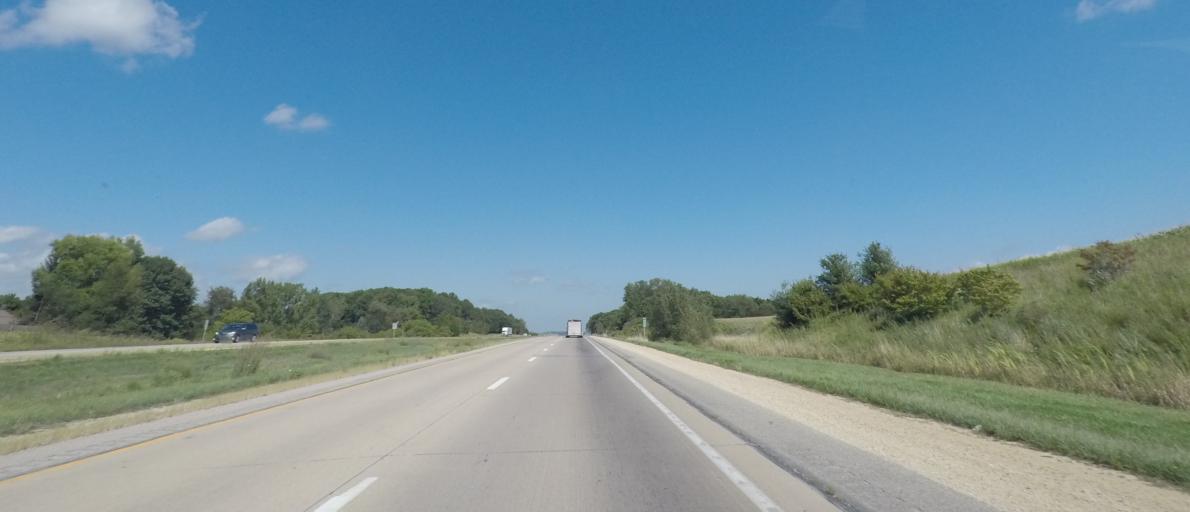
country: US
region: Iowa
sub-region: Jones County
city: Anamosa
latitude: 42.0750
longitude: -91.2849
